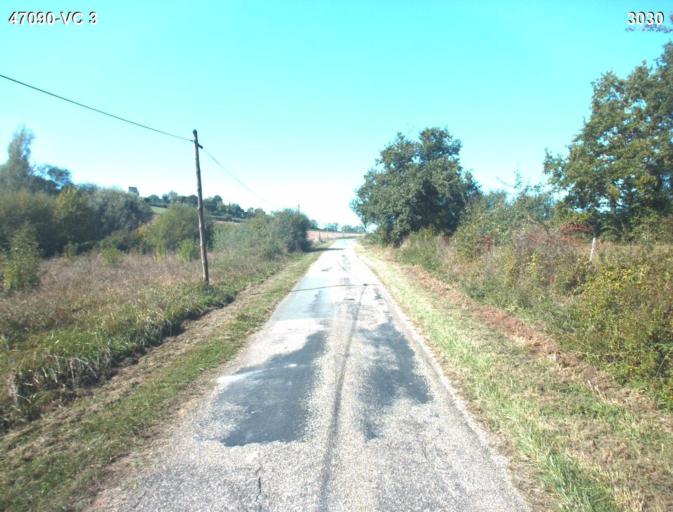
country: FR
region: Aquitaine
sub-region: Departement du Lot-et-Garonne
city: Nerac
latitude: 44.1714
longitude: 0.3841
